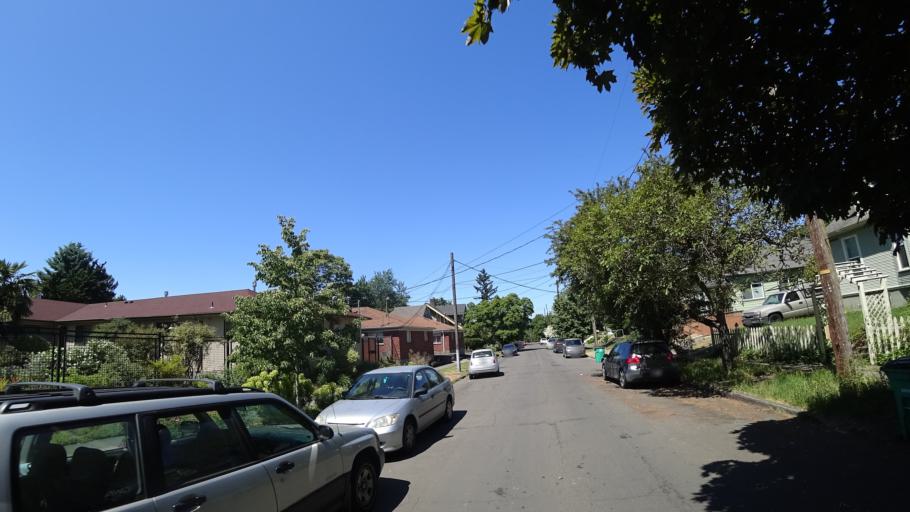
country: US
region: Oregon
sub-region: Multnomah County
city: Portland
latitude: 45.5644
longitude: -122.6552
